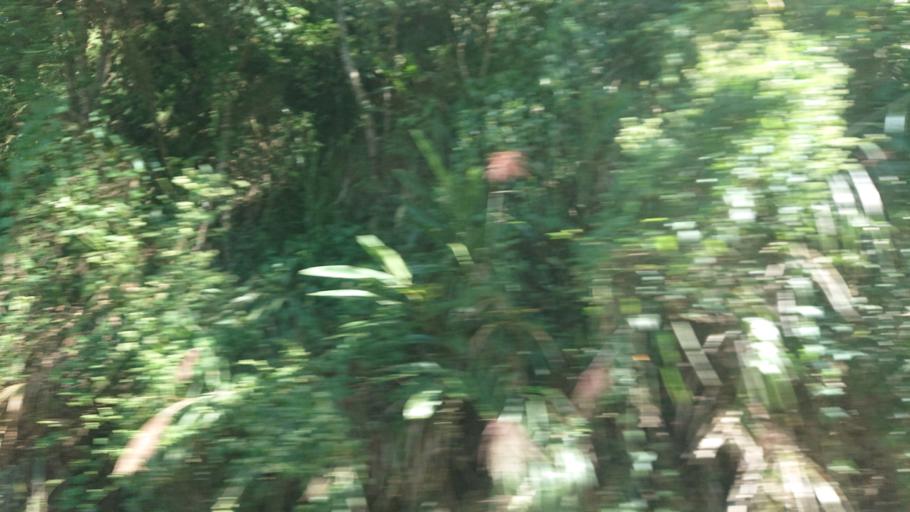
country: TW
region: Taiwan
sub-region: Chiayi
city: Jiayi Shi
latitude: 23.5268
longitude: 120.6277
